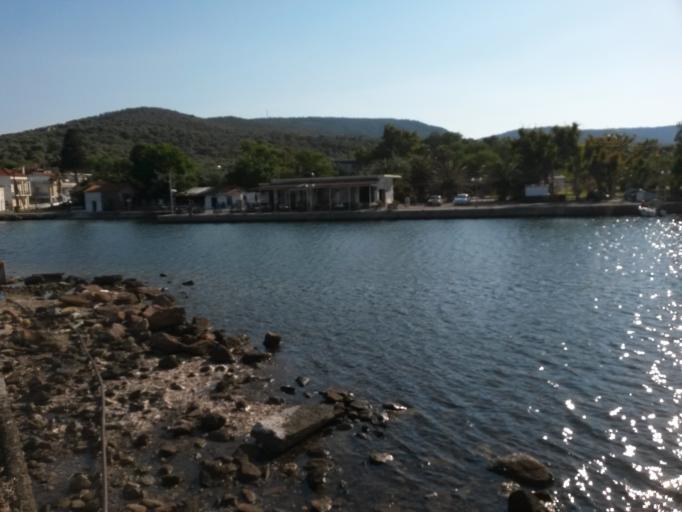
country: GR
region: North Aegean
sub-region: Nomos Lesvou
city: Pamfylla
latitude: 39.1813
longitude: 26.5004
